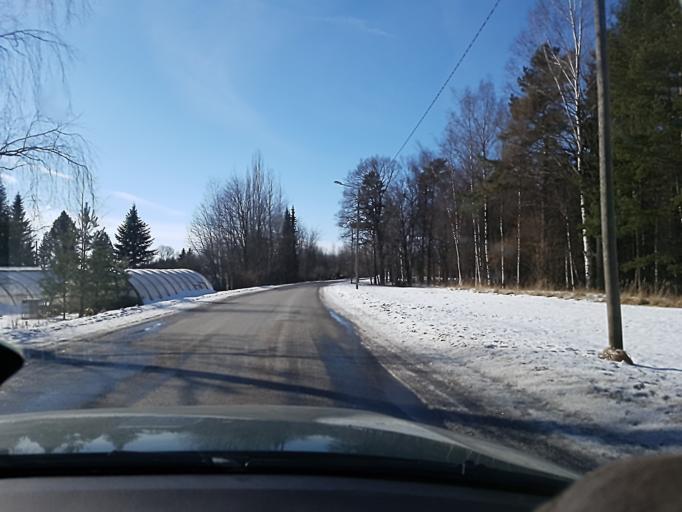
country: FI
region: Uusimaa
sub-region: Helsinki
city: Lohja
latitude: 60.1791
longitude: 23.9883
